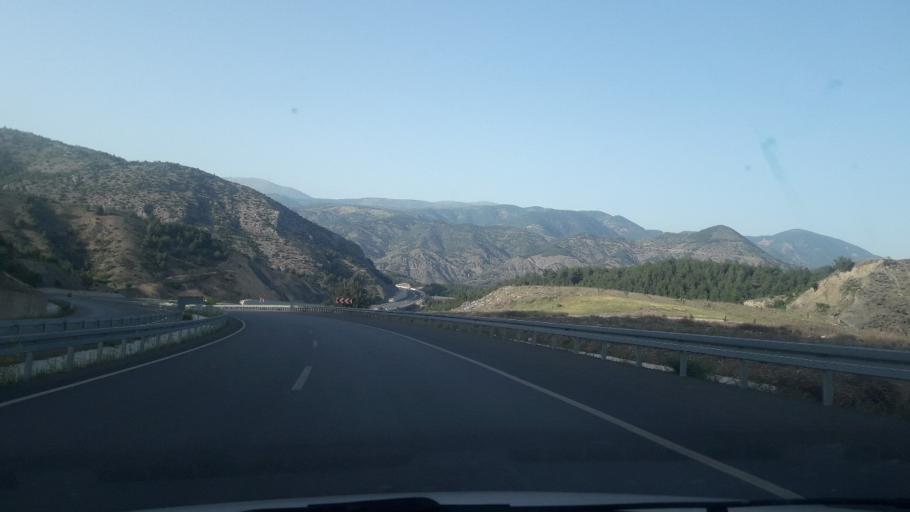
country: TR
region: Amasya
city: Amasya
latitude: 40.6724
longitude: 35.8028
